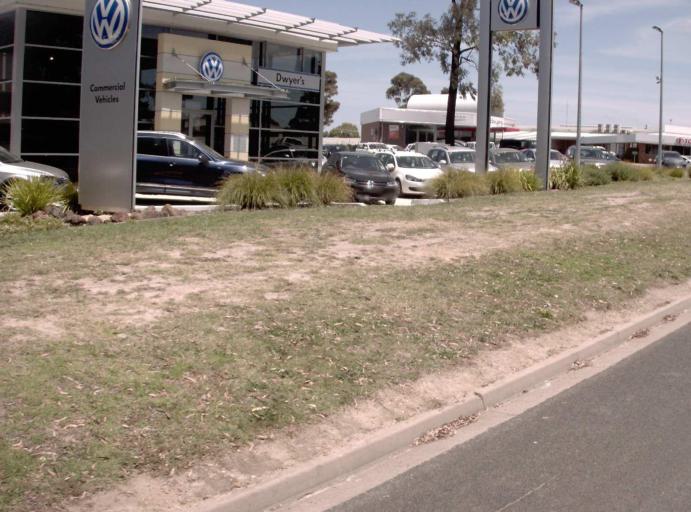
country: AU
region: Victoria
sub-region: East Gippsland
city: Bairnsdale
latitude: -37.8321
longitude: 147.6092
